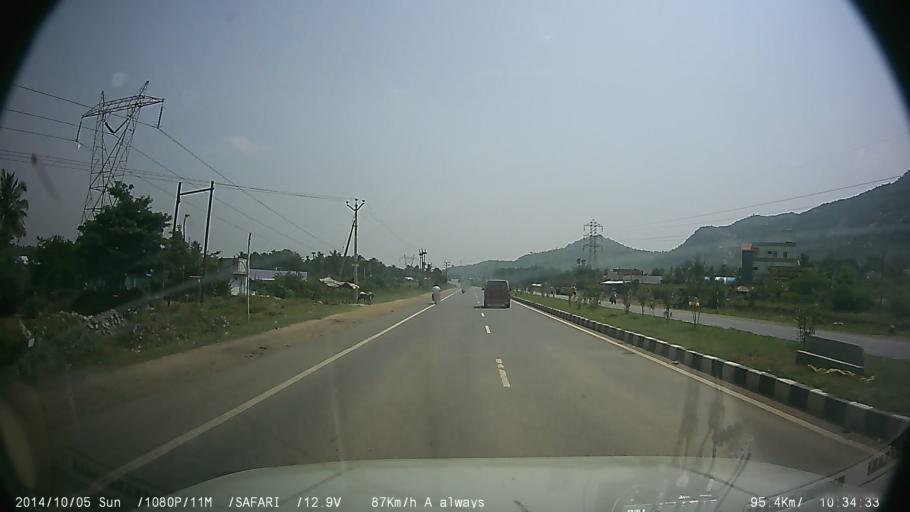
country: IN
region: Tamil Nadu
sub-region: Salem
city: Salem
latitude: 11.6521
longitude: 78.1931
